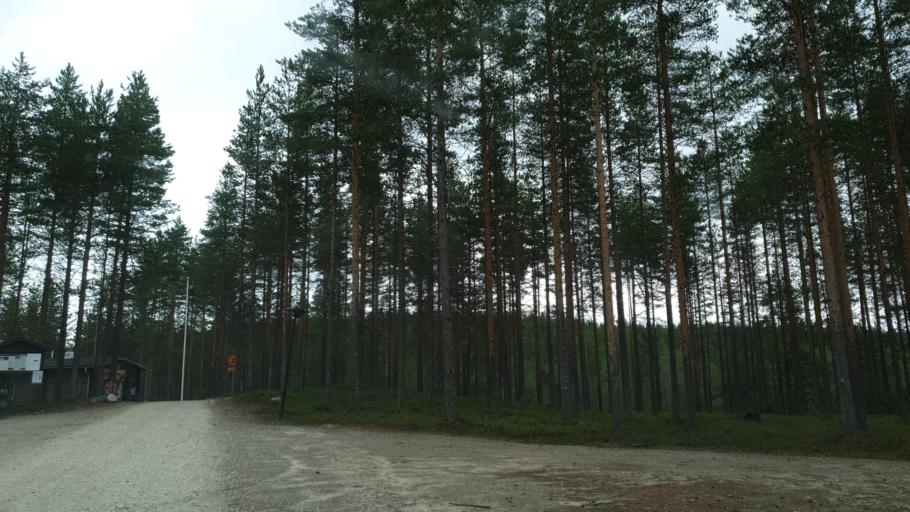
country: FI
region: Kainuu
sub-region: Kehys-Kainuu
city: Kuhmo
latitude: 64.1928
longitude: 29.1976
